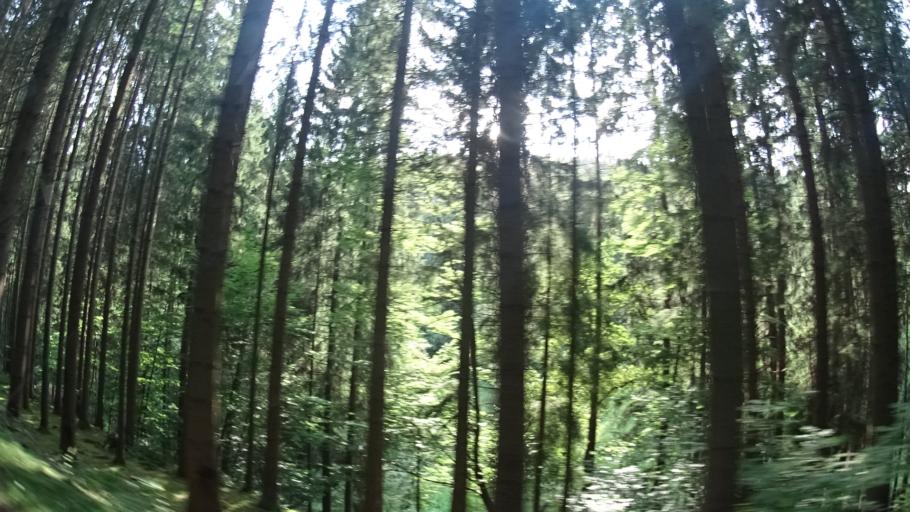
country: DE
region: Hesse
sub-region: Regierungsbezirk Darmstadt
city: Hesseneck
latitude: 49.5745
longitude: 9.0749
